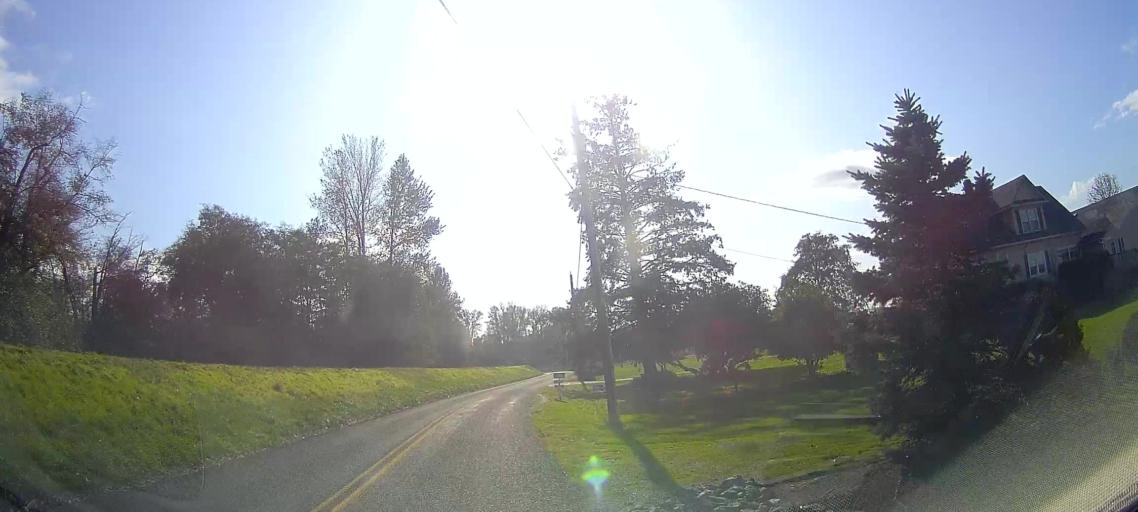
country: US
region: Washington
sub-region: Skagit County
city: Mount Vernon
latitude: 48.3382
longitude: -122.3516
